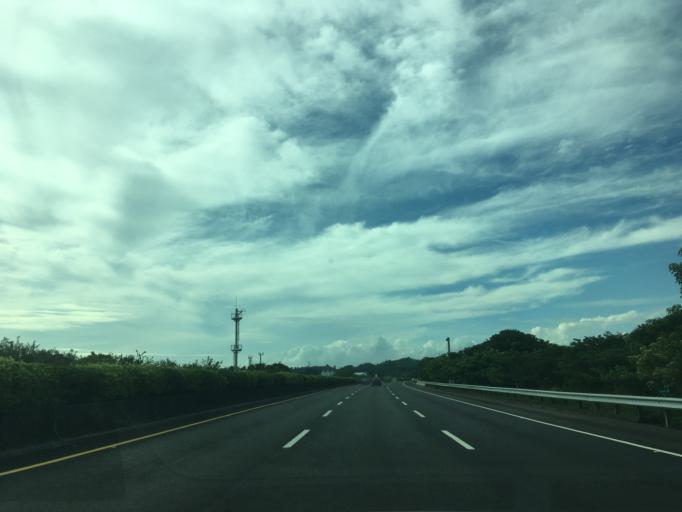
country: TW
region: Taiwan
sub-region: Chiayi
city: Jiayi Shi
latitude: 23.5115
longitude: 120.4864
